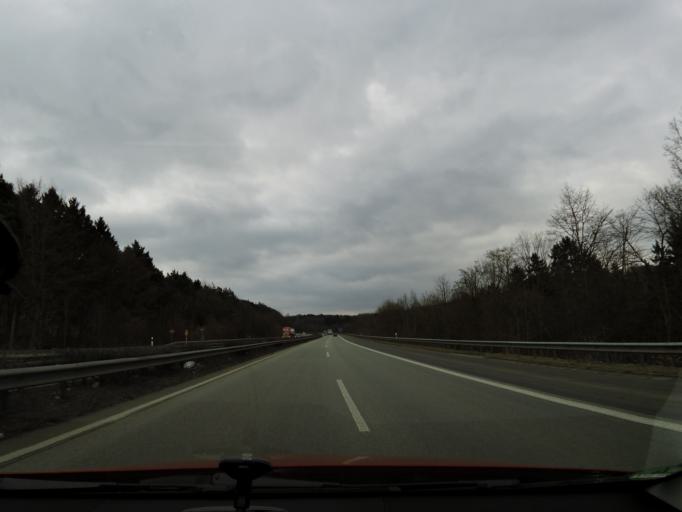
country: DE
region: Rheinland-Pfalz
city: Hilgert
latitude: 50.4472
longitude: 7.6794
